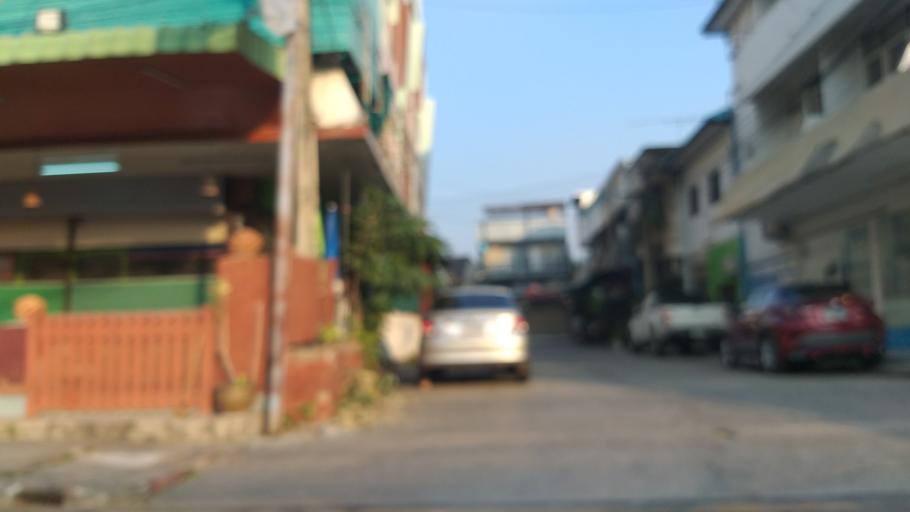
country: TH
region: Khon Kaen
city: Khon Kaen
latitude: 16.4222
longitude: 102.8331
